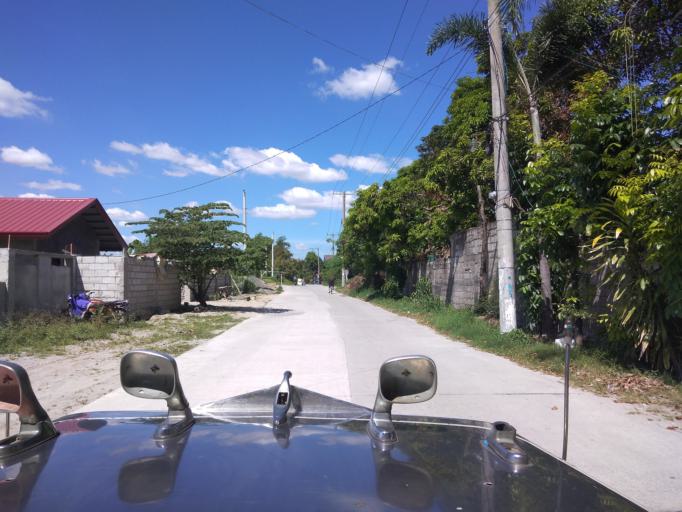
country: PH
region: Central Luzon
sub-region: Province of Pampanga
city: Magliman
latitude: 15.0290
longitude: 120.6502
